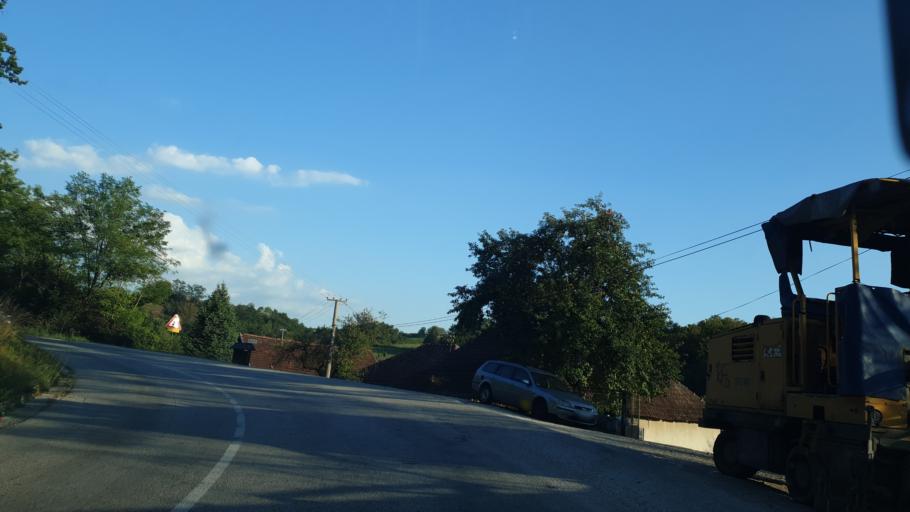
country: RS
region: Central Serbia
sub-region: Zlatiborski Okrug
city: Pozega
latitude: 43.9500
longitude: 20.0246
